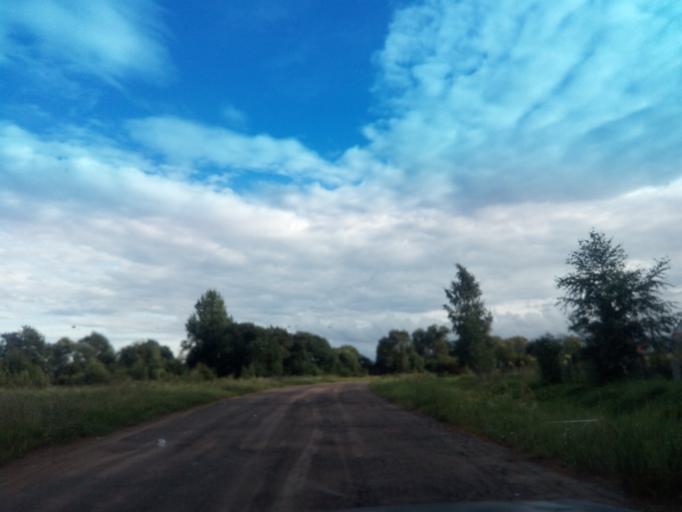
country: BY
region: Vitebsk
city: Dzisna
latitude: 55.6741
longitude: 28.3499
